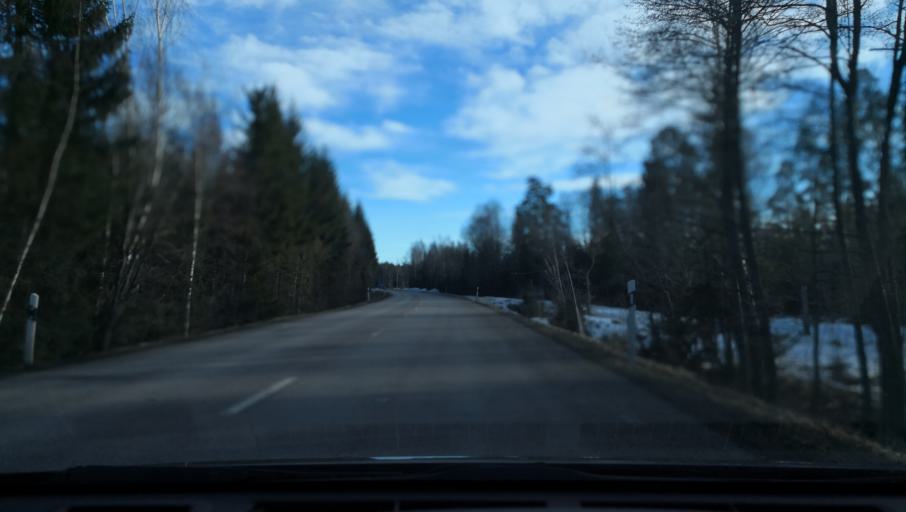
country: SE
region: Uppsala
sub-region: Osthammars Kommun
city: Osterbybruk
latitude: 60.1771
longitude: 17.9173
